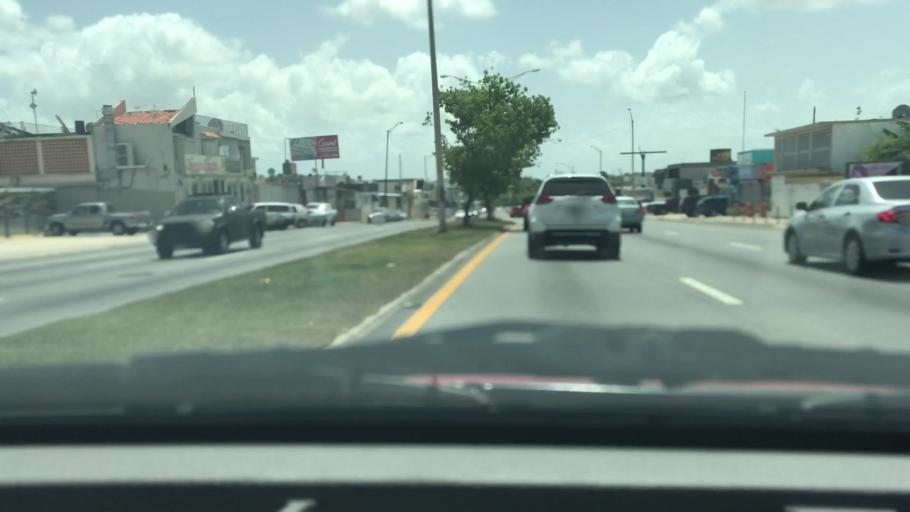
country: PR
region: Bayamon
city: Bayamon
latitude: 18.3653
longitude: -66.1741
